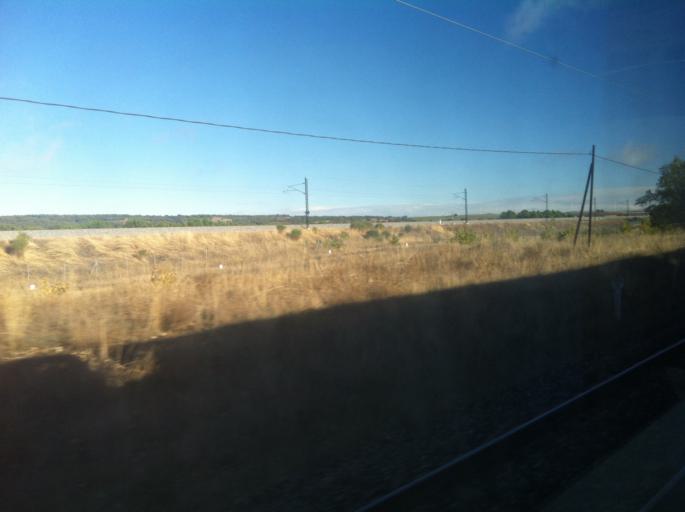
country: ES
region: Castille and Leon
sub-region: Provincia de Palencia
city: Villodrigo
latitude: 42.1596
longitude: -4.0843
